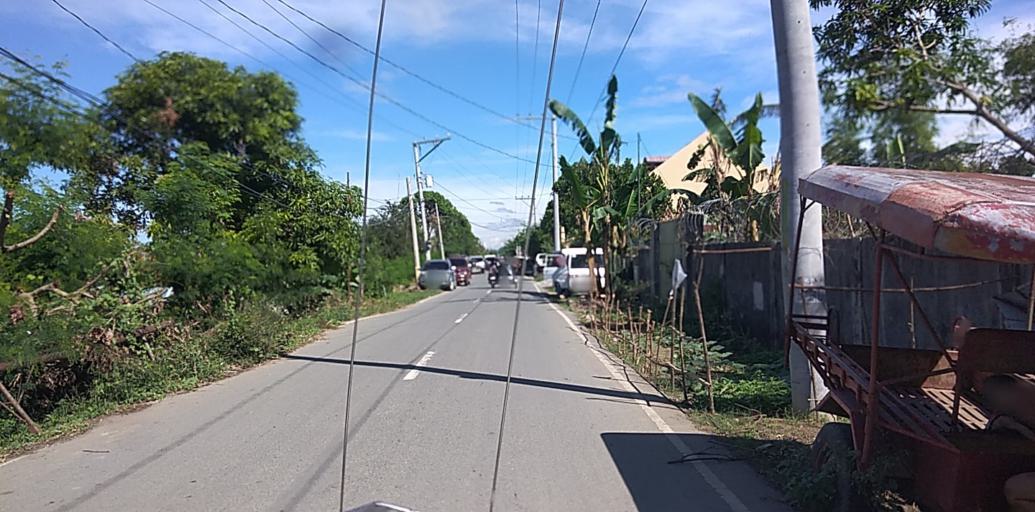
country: PH
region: Central Luzon
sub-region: Province of Pampanga
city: Candaba
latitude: 15.0916
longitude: 120.8118
